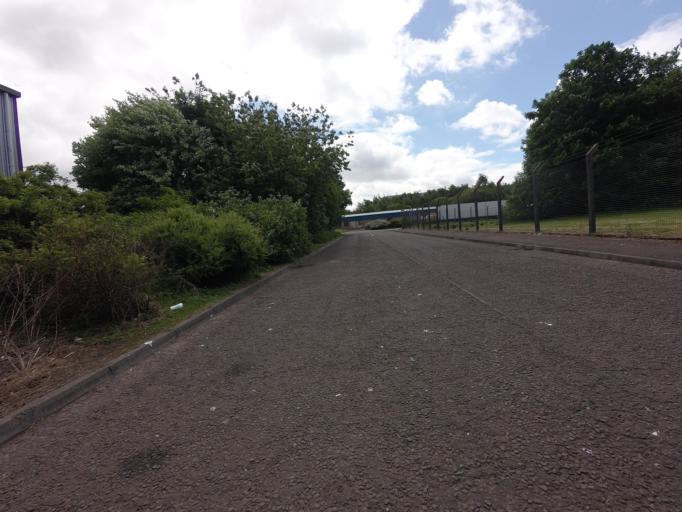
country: GB
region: Scotland
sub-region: West Lothian
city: Livingston
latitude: 55.9150
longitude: -3.5141
